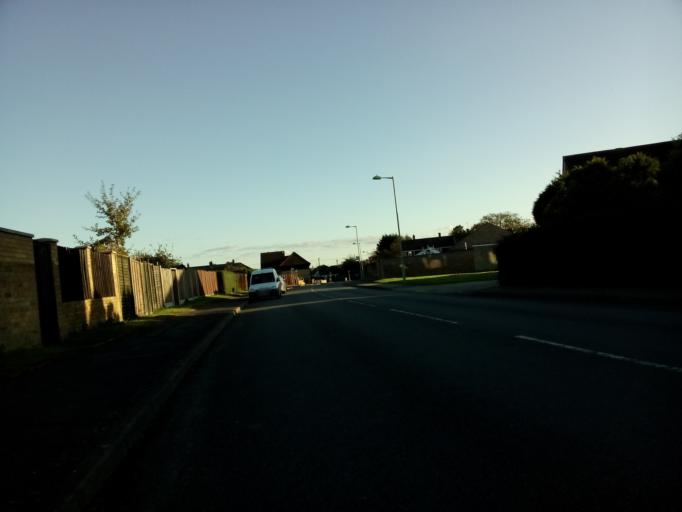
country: GB
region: England
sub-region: Suffolk
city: Sudbury
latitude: 52.0319
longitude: 0.7449
